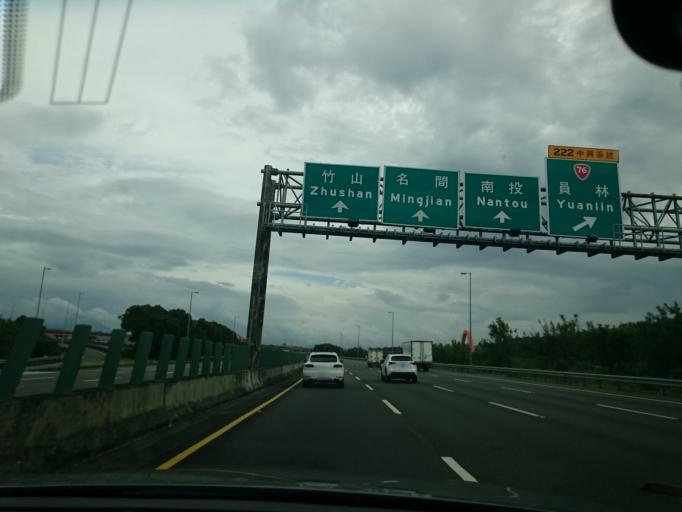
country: TW
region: Taiwan
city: Zhongxing New Village
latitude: 23.9630
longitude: 120.6503
